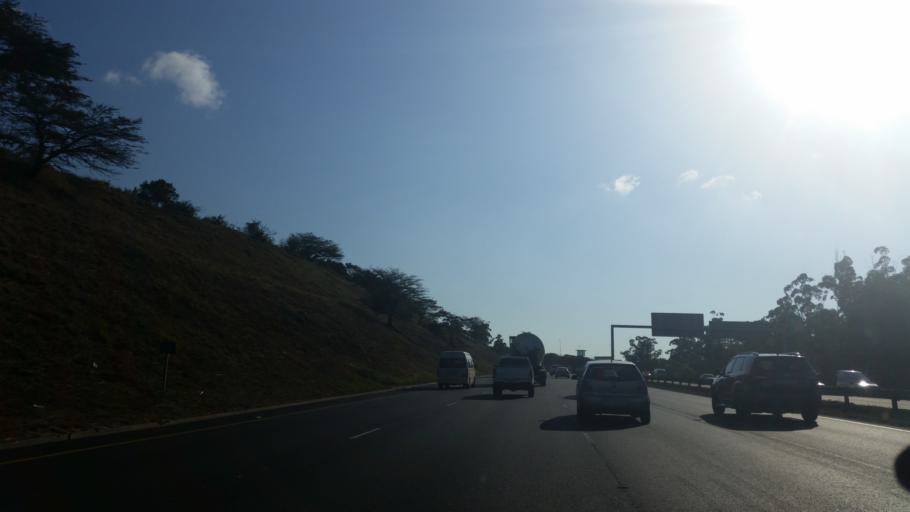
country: ZA
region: KwaZulu-Natal
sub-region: eThekwini Metropolitan Municipality
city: Berea
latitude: -29.8340
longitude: 30.9597
